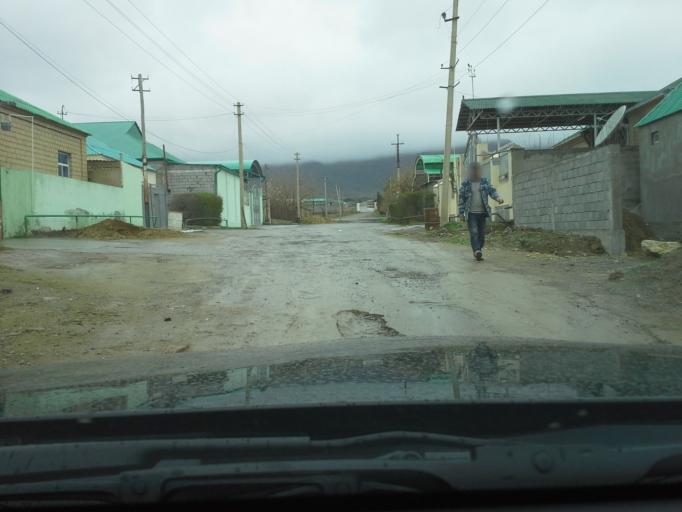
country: TM
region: Ahal
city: Abadan
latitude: 37.9676
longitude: 58.2064
